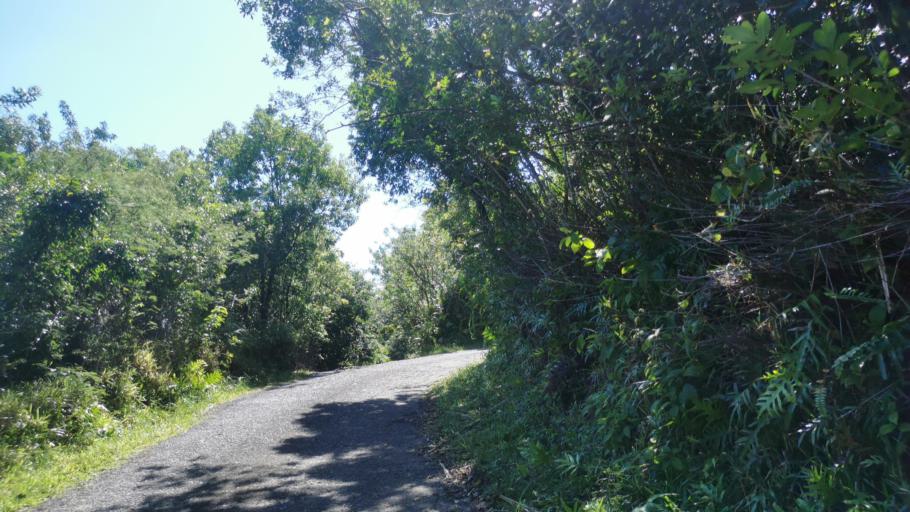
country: RE
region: Reunion
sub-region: Reunion
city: Saint-Philippe
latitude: -21.3578
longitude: 55.7395
